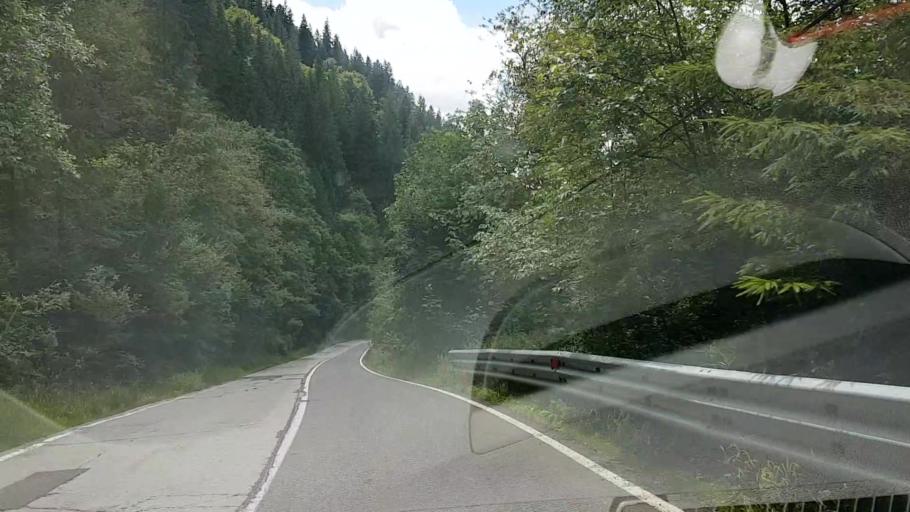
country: RO
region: Suceava
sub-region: Comuna Crucea
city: Crucea
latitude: 47.3795
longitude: 25.5878
